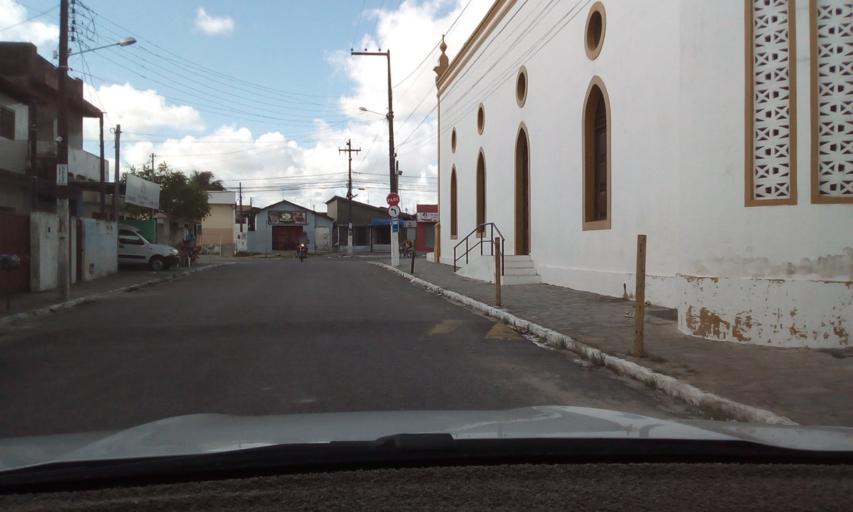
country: BR
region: Paraiba
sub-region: Bayeux
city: Bayeux
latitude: -7.1240
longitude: -34.9186
